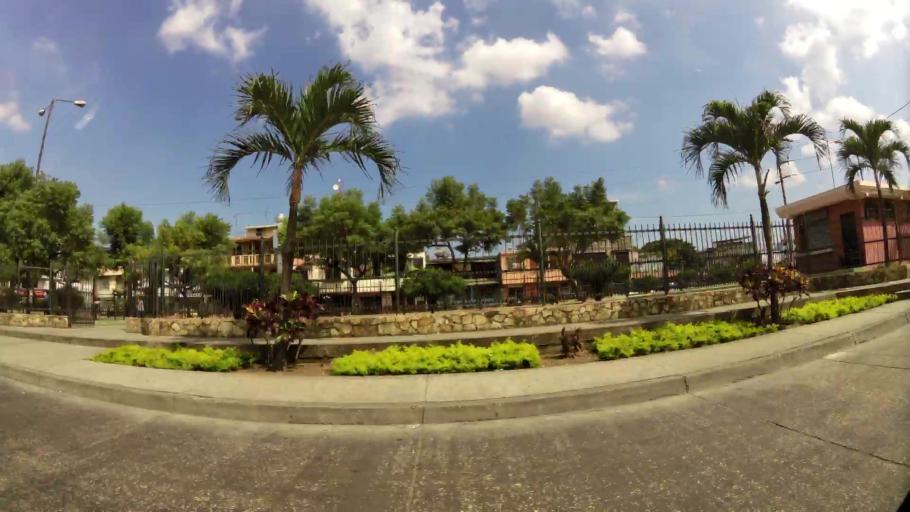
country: EC
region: Guayas
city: Guayaquil
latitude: -2.1286
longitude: -79.9376
